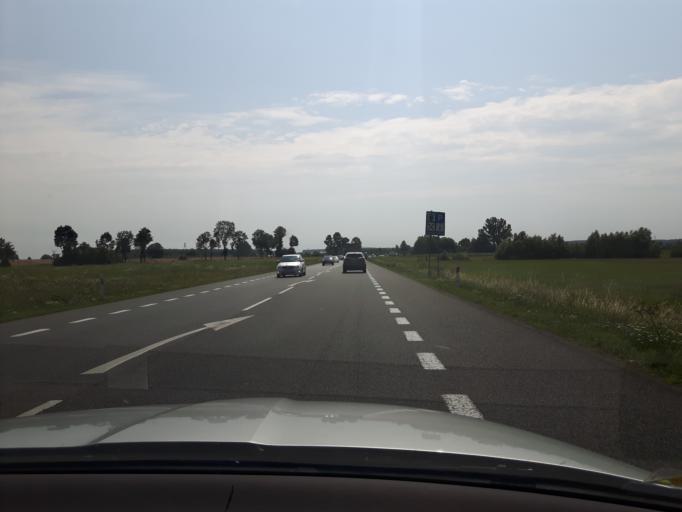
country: PL
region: Masovian Voivodeship
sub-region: Powiat mlawski
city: Wieczfnia Koscielna
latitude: 53.1820
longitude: 20.4297
